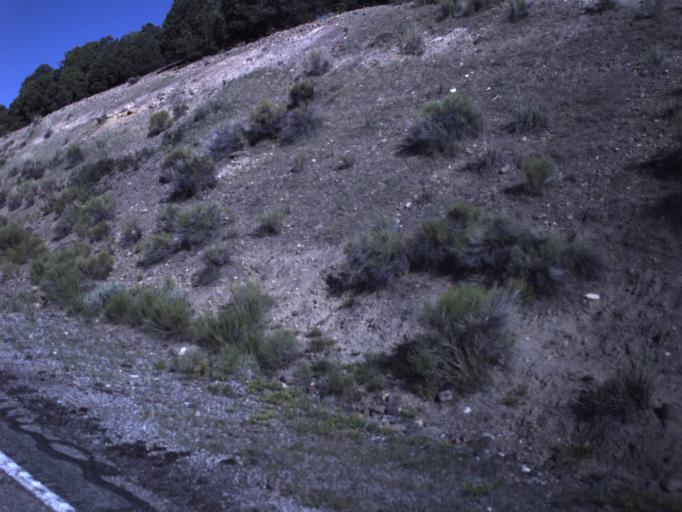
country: US
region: Utah
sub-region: Wayne County
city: Loa
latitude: 38.6489
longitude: -111.4419
